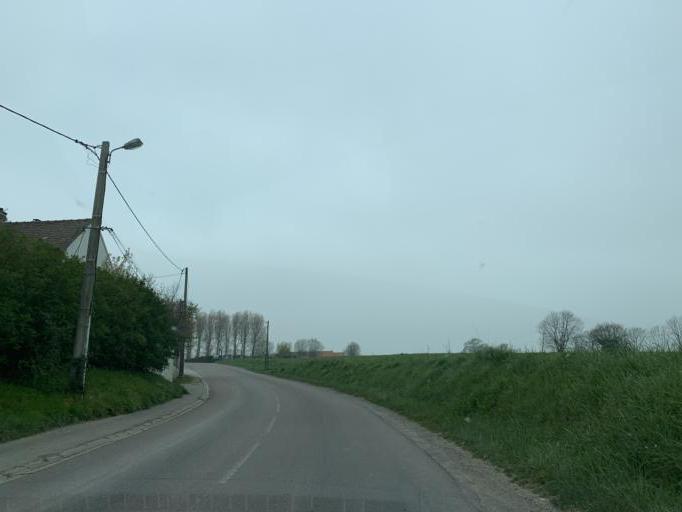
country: FR
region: Nord-Pas-de-Calais
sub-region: Departement du Pas-de-Calais
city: Rinxent
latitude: 50.7798
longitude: 1.7372
